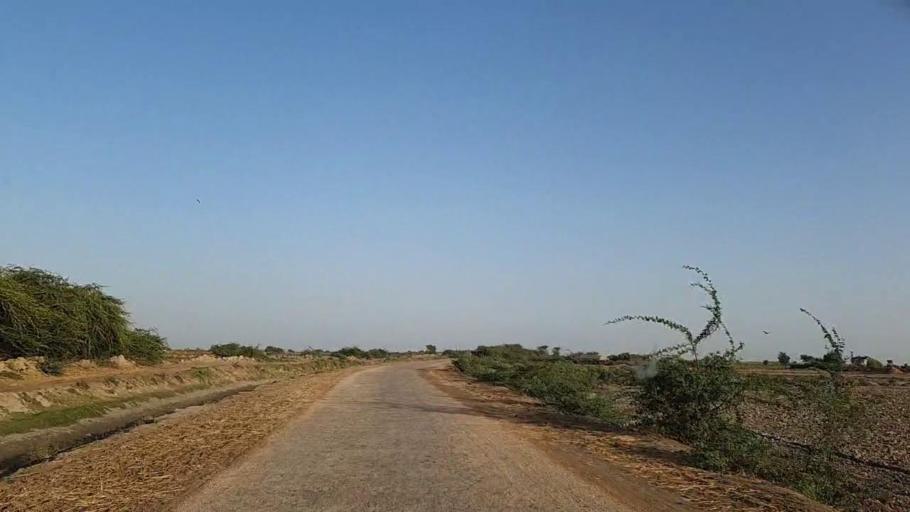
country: PK
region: Sindh
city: Jati
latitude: 24.4064
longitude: 68.3533
